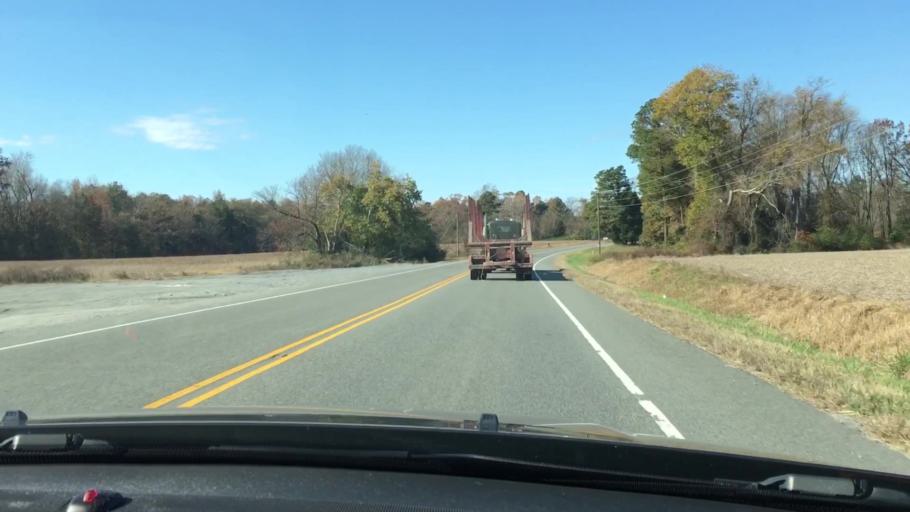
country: US
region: Virginia
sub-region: King William County
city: Central Garage
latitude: 37.7632
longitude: -77.1494
